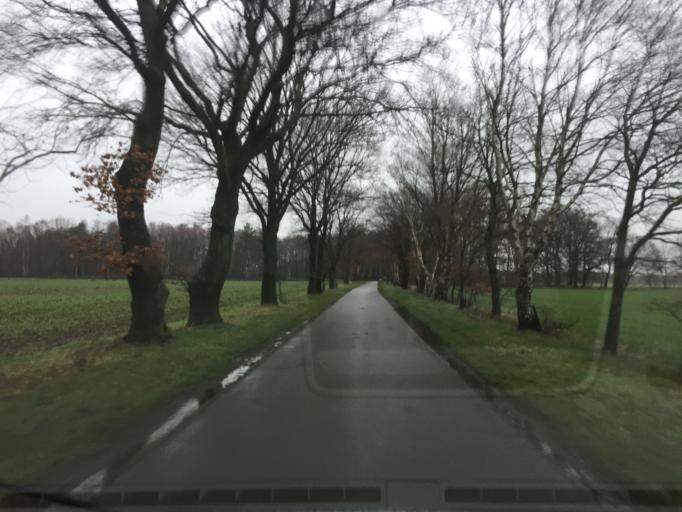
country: DE
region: Lower Saxony
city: Siedenburg
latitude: 52.6432
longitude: 8.9238
